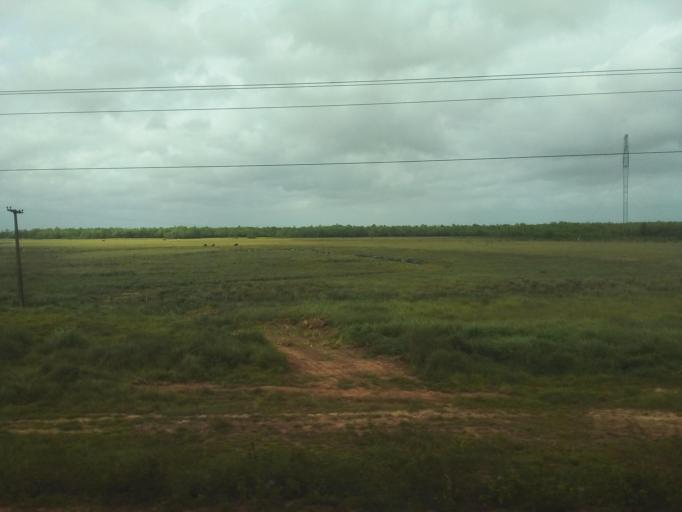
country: BR
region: Maranhao
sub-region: Icatu
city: Icatu
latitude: -2.9119
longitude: -44.3559
